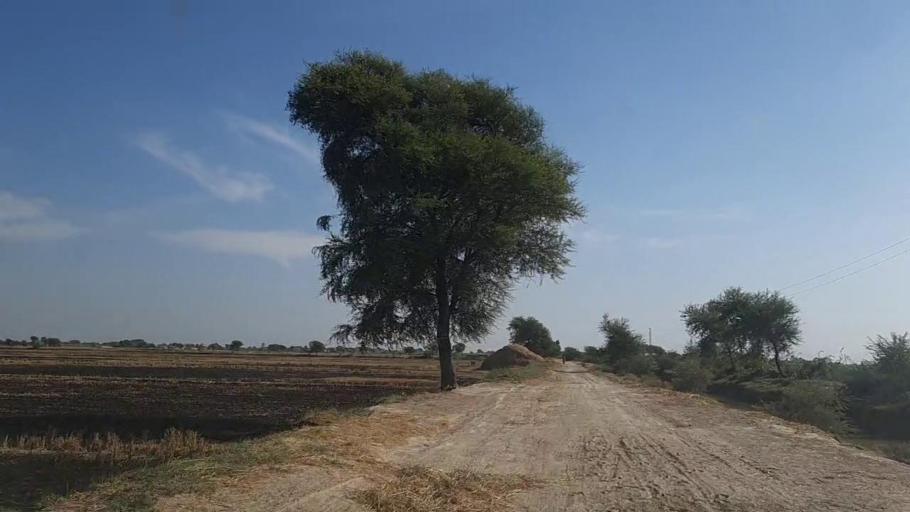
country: PK
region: Sindh
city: Bulri
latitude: 24.8662
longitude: 68.2834
